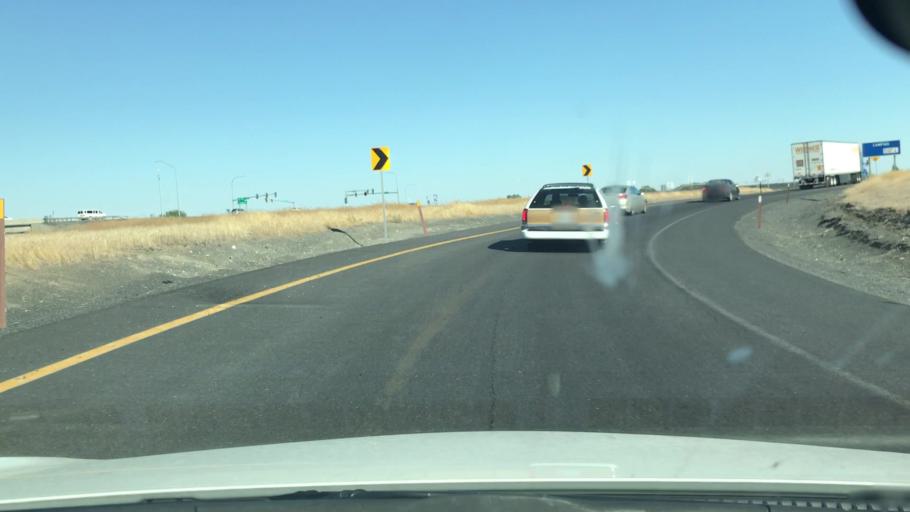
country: US
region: Washington
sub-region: Grant County
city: Moses Lake
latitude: 47.0988
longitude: -119.2457
